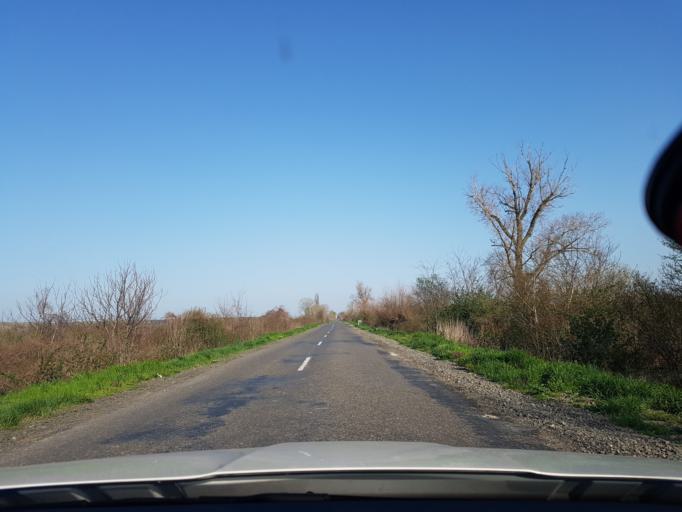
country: HU
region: Tolna
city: Ocseny
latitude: 46.3397
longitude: 18.7673
